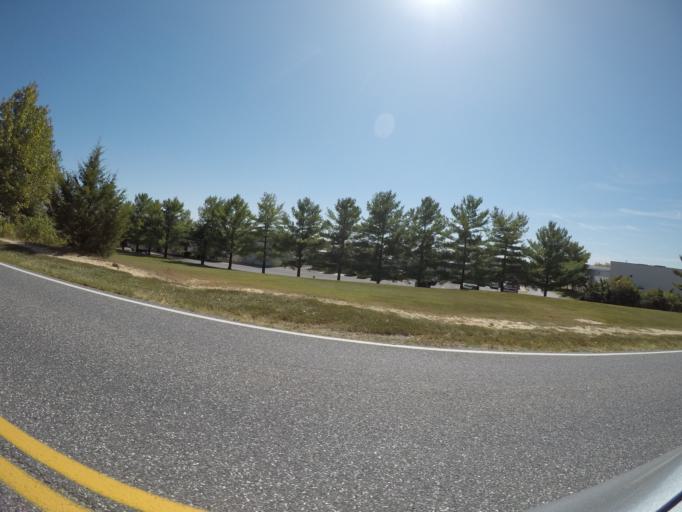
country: US
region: Maryland
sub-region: Harford County
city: Aberdeen
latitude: 39.5263
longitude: -76.1820
